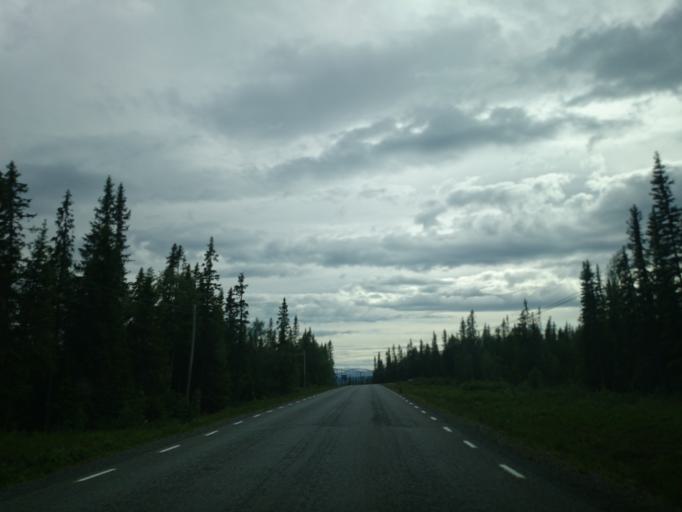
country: SE
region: Jaemtland
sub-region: Are Kommun
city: Are
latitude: 63.2308
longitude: 13.1615
